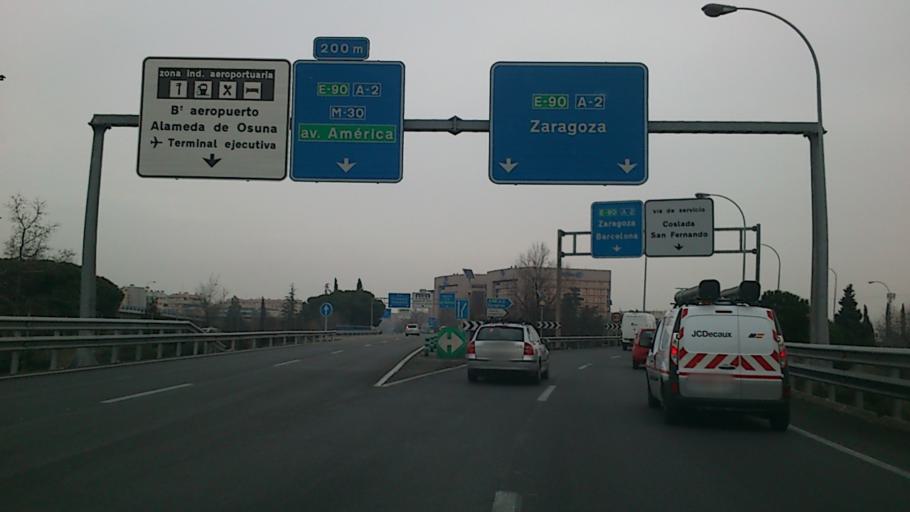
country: ES
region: Madrid
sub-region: Provincia de Madrid
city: Barajas de Madrid
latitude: 40.4488
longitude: -3.5881
